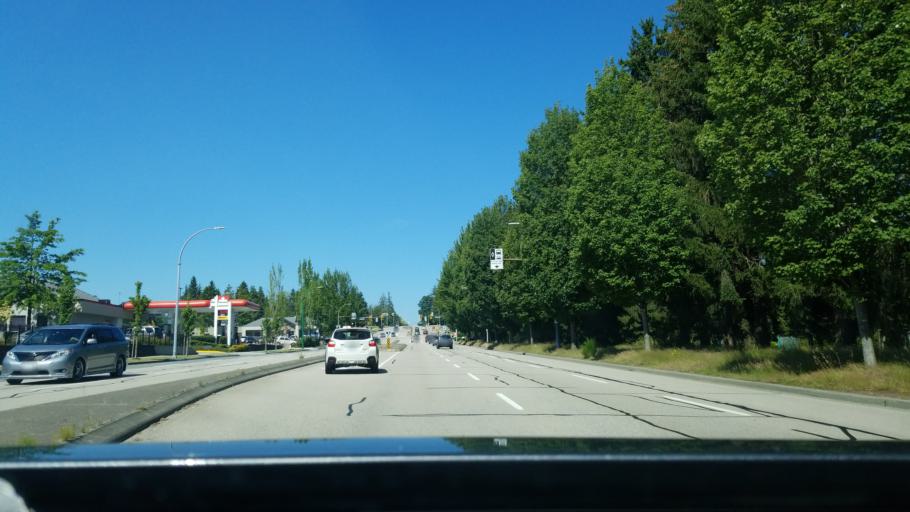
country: CA
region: British Columbia
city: Burnaby
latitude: 49.2804
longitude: -122.9669
